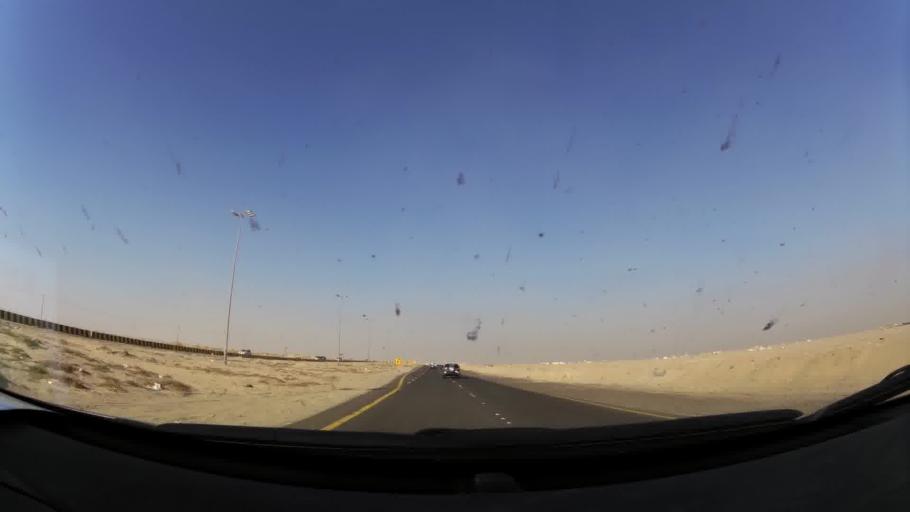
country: KW
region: Al Ahmadi
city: Al Ahmadi
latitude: 28.8696
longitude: 48.0751
